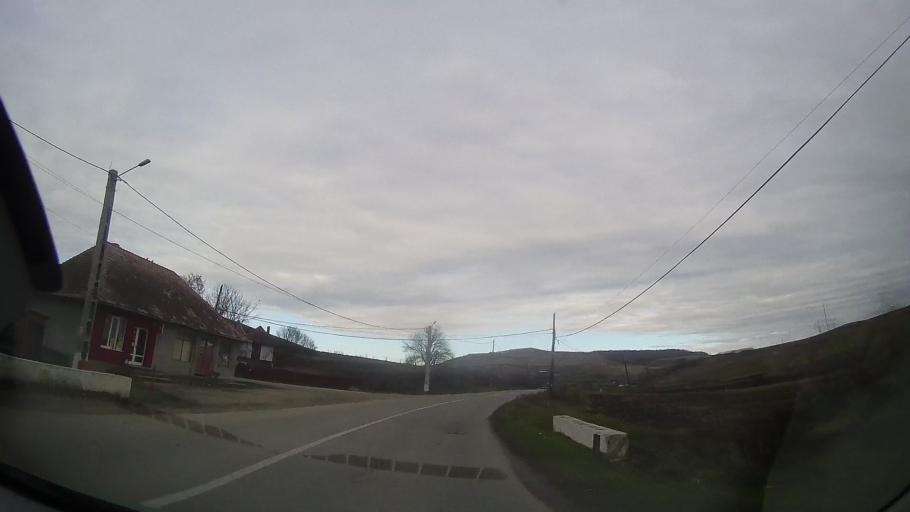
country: RO
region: Cluj
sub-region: Comuna Camarasu
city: Camarasu
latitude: 46.8190
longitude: 24.1365
